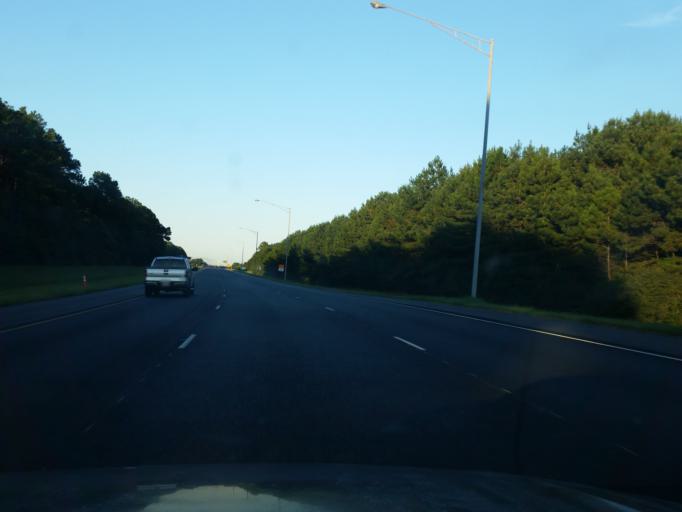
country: US
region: Alabama
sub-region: Mobile County
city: Tillmans Corner
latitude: 30.6265
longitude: -88.1174
